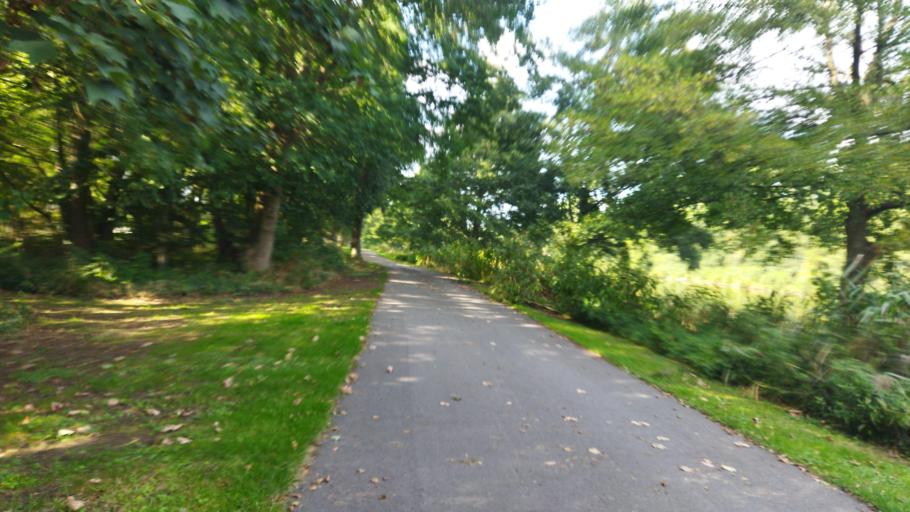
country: DE
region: Lower Saxony
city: Walchum
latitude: 52.9268
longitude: 7.2970
